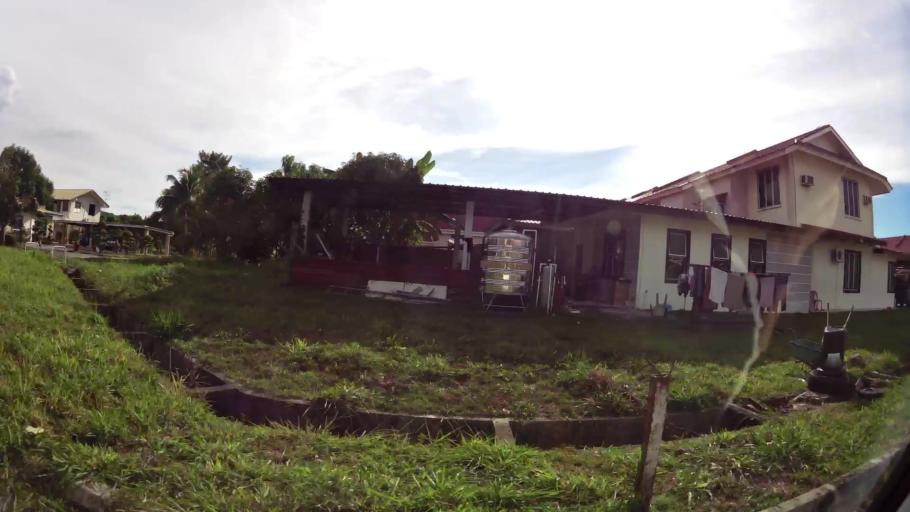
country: BN
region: Brunei and Muara
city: Bandar Seri Begawan
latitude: 4.9734
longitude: 115.0285
